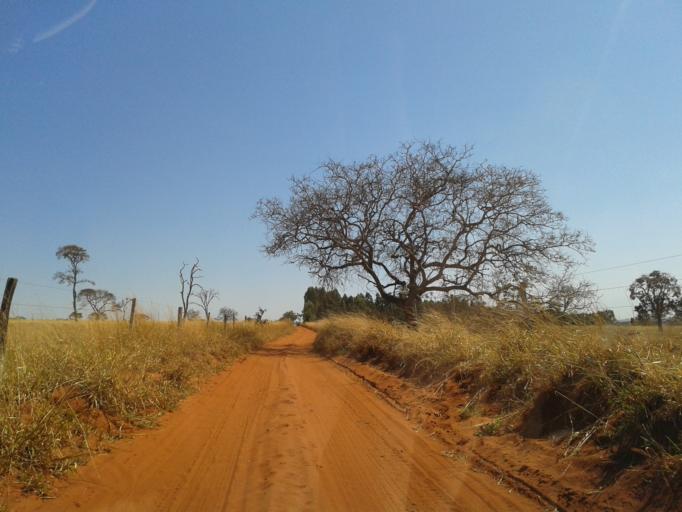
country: BR
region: Minas Gerais
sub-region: Ituiutaba
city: Ituiutaba
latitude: -19.0233
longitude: -49.2156
